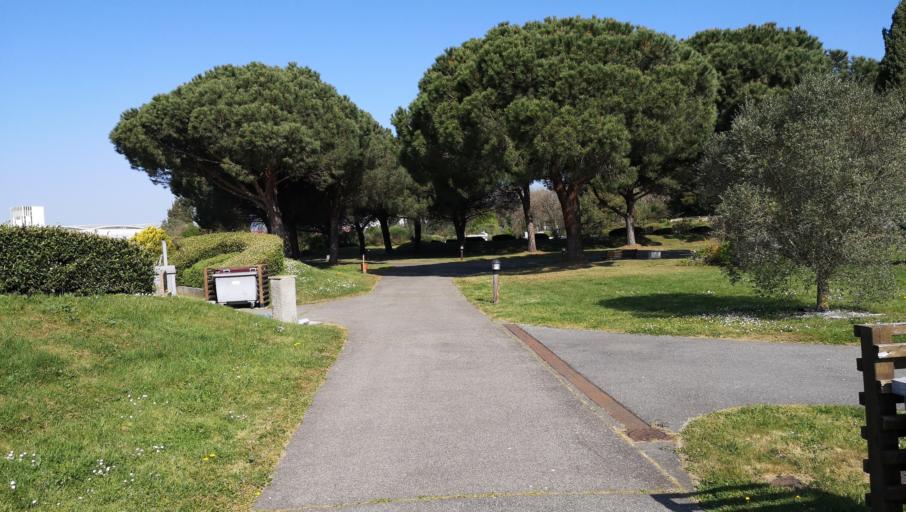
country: FR
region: Midi-Pyrenees
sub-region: Departement de la Haute-Garonne
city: Beauzelle
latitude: 43.6513
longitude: 1.3687
